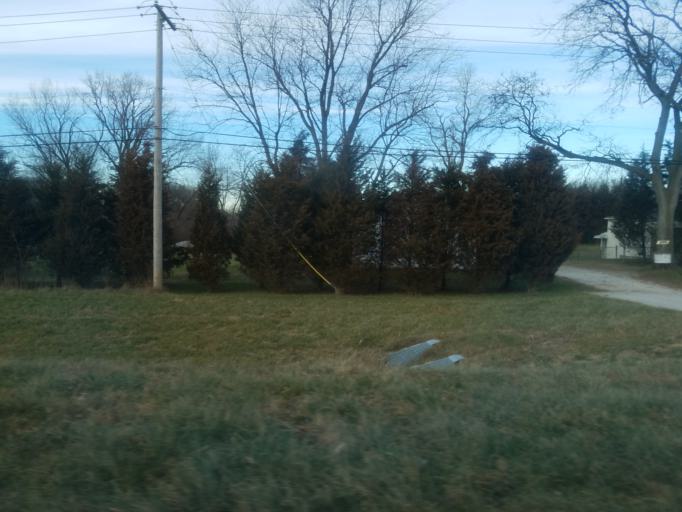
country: US
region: Illinois
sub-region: Cook County
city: Lemont
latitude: 41.6275
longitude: -88.0076
